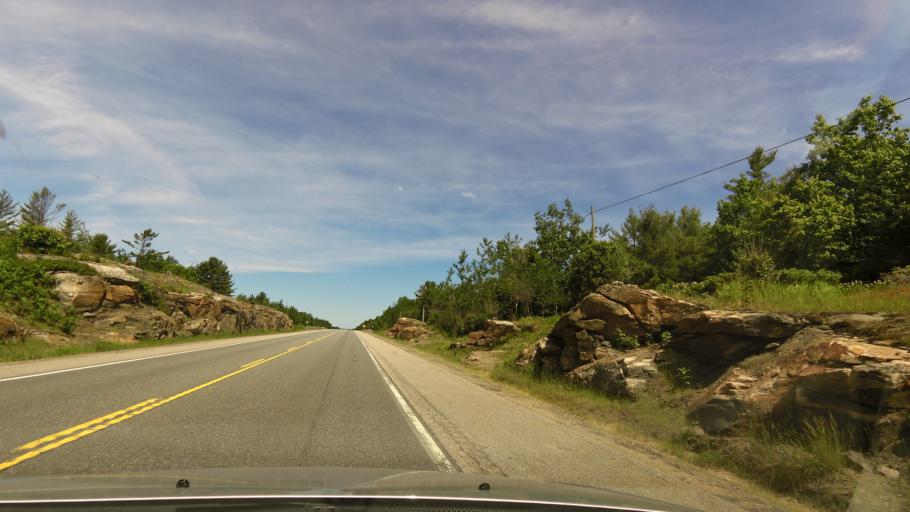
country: CA
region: Ontario
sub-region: Parry Sound District
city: Parry Sound
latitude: 45.4689
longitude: -80.1674
